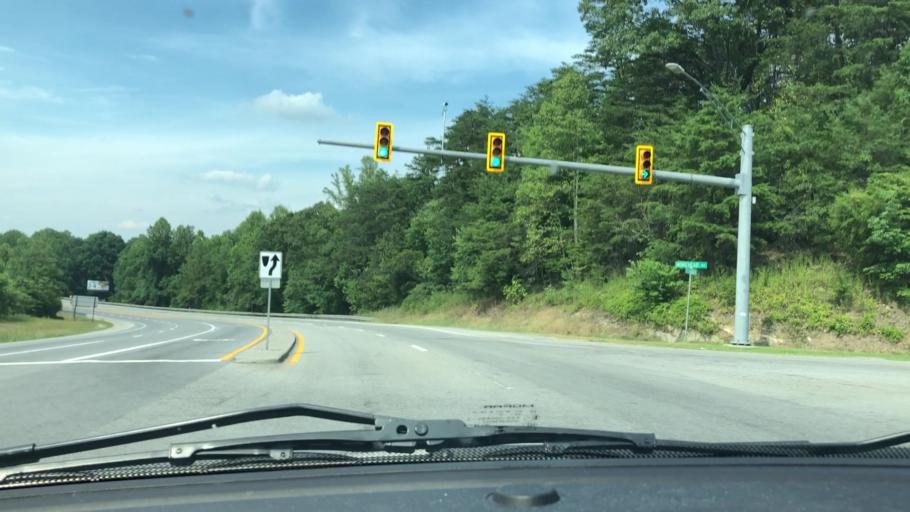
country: US
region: Virginia
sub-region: Henry County
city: Chatmoss
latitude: 36.5789
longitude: -79.8630
